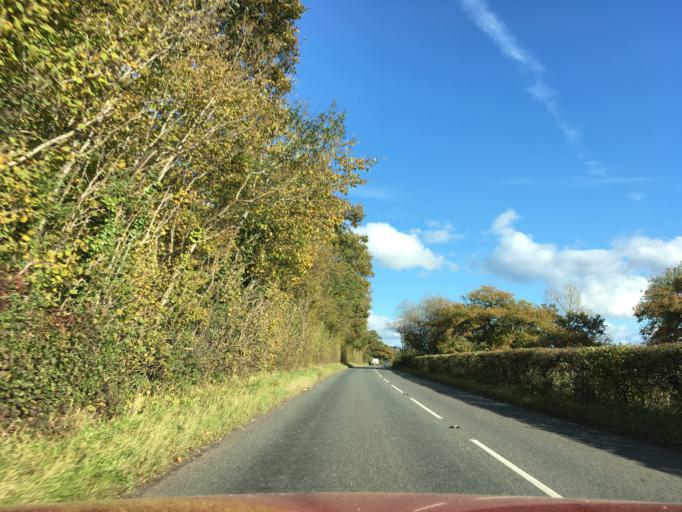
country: GB
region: Wales
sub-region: Sir Powys
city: Brecon
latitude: 51.9605
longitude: -3.3702
